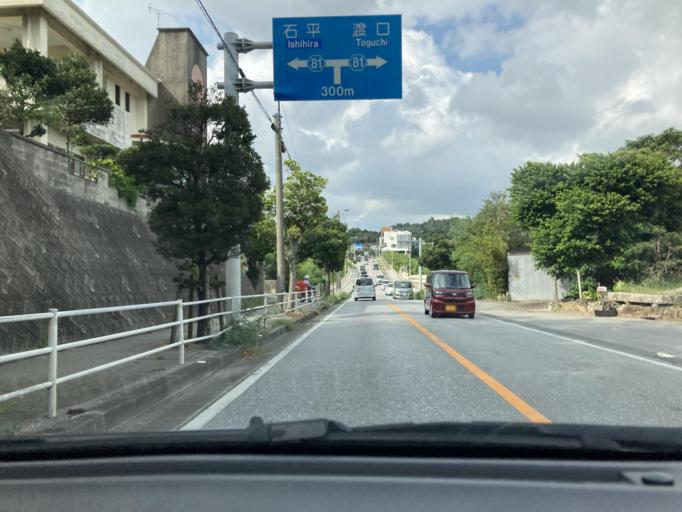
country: JP
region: Okinawa
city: Chatan
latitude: 26.2932
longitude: 127.7846
